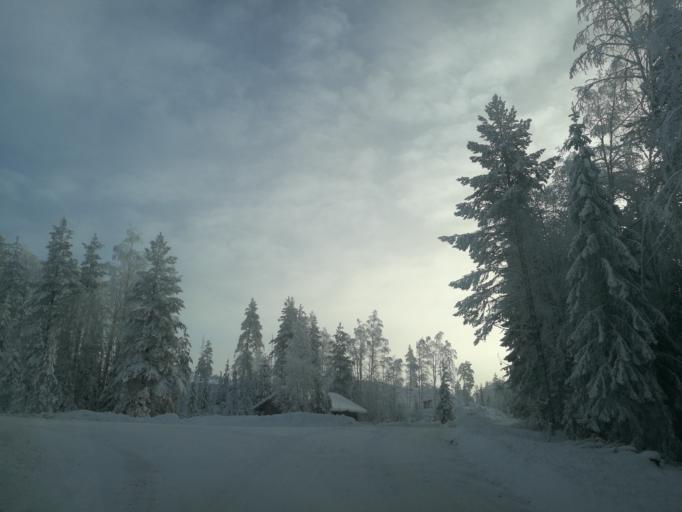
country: SE
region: Vaermland
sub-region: Torsby Kommun
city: Torsby
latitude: 60.6404
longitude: 12.7888
